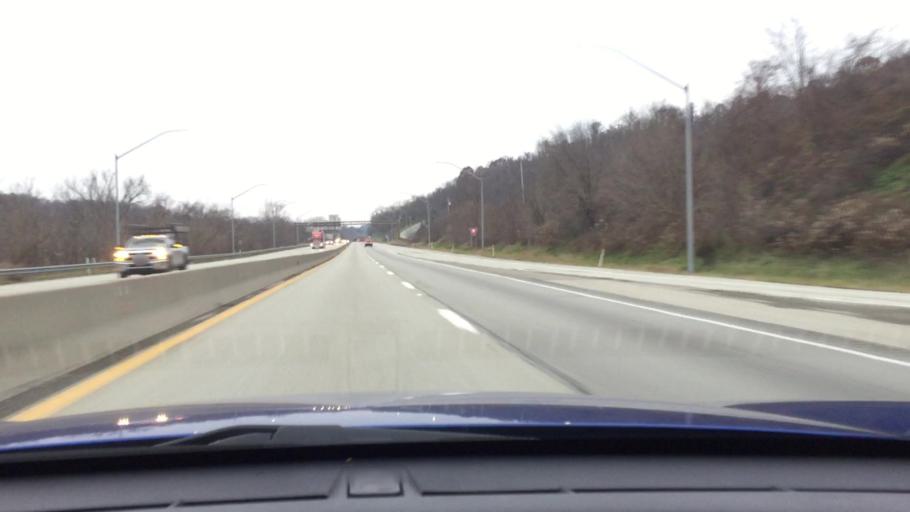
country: US
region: Pennsylvania
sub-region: Washington County
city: Charleroi
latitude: 40.1114
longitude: -79.9261
